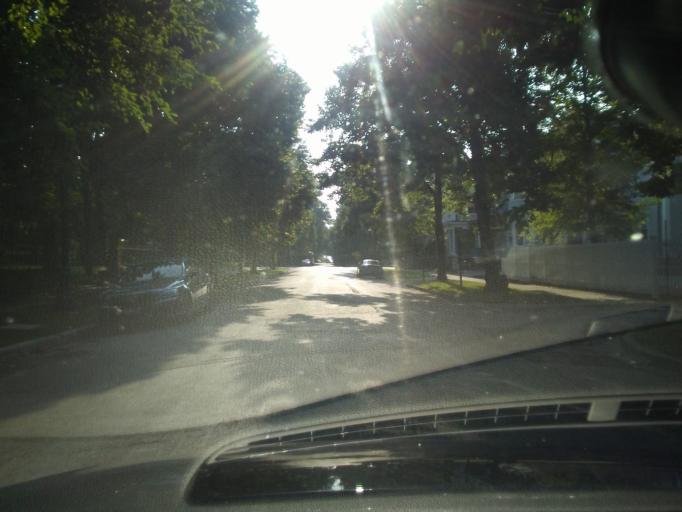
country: US
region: Illinois
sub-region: Cook County
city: Evanston
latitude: 42.0376
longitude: -87.6761
